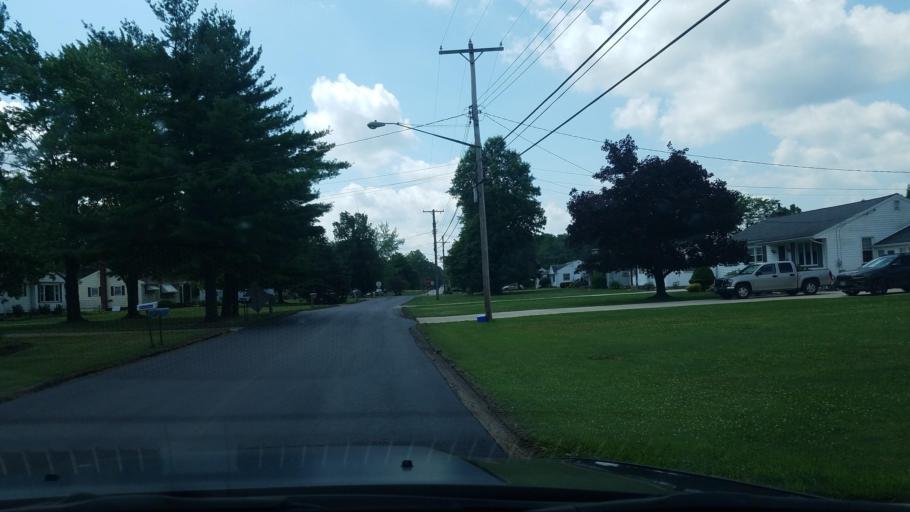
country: US
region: Ohio
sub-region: Trumbull County
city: Champion Heights
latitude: 41.2977
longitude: -80.8628
